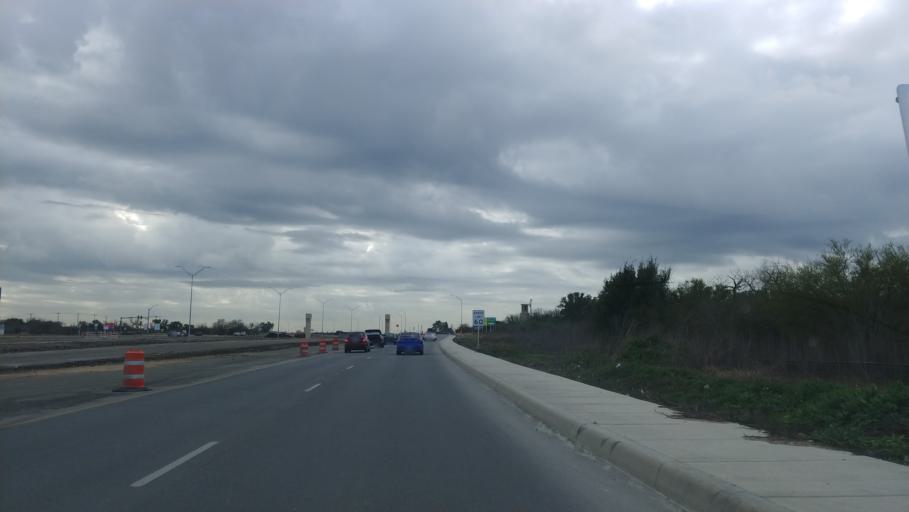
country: US
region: Texas
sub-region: Bexar County
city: Lackland Air Force Base
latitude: 29.4135
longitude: -98.7103
